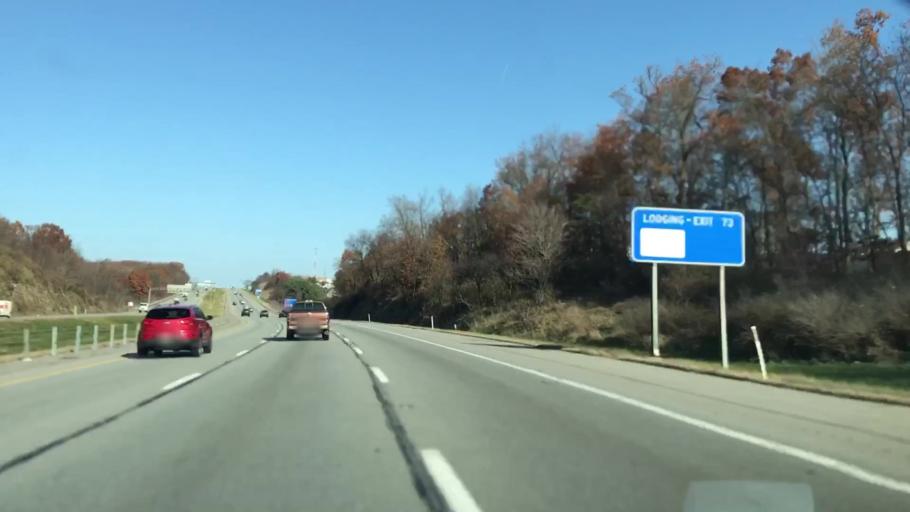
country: US
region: Pennsylvania
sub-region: Allegheny County
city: Franklin Park
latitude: 40.5990
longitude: -80.0933
